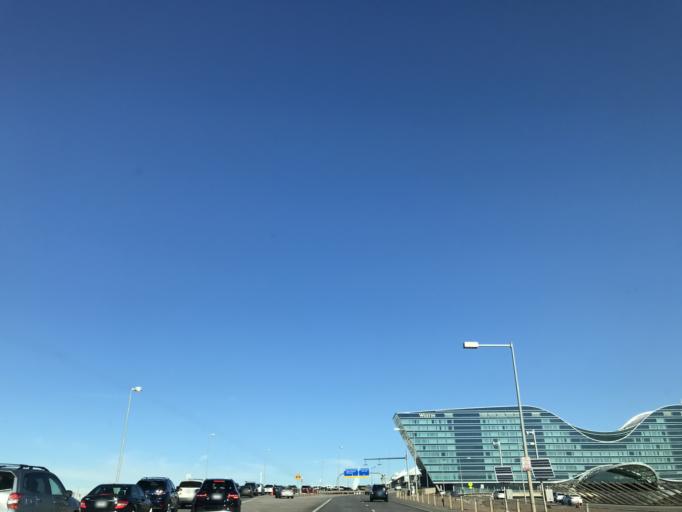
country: US
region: Colorado
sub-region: Weld County
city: Lochbuie
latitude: 39.8450
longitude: -104.6753
